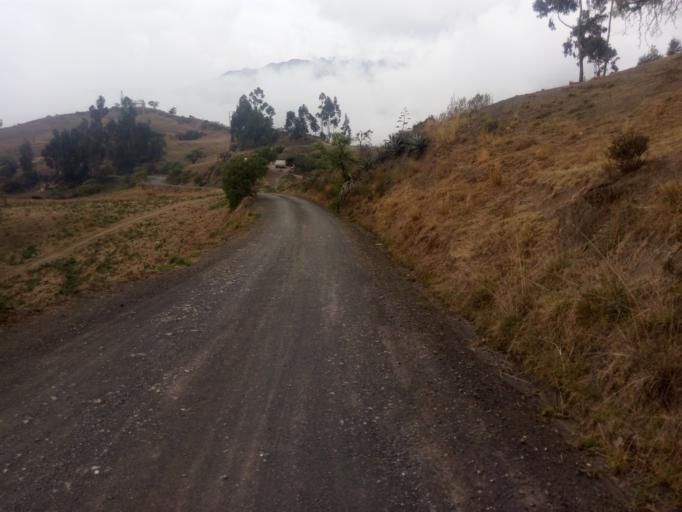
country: CO
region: Boyaca
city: Chita
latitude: 6.1917
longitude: -72.4907
